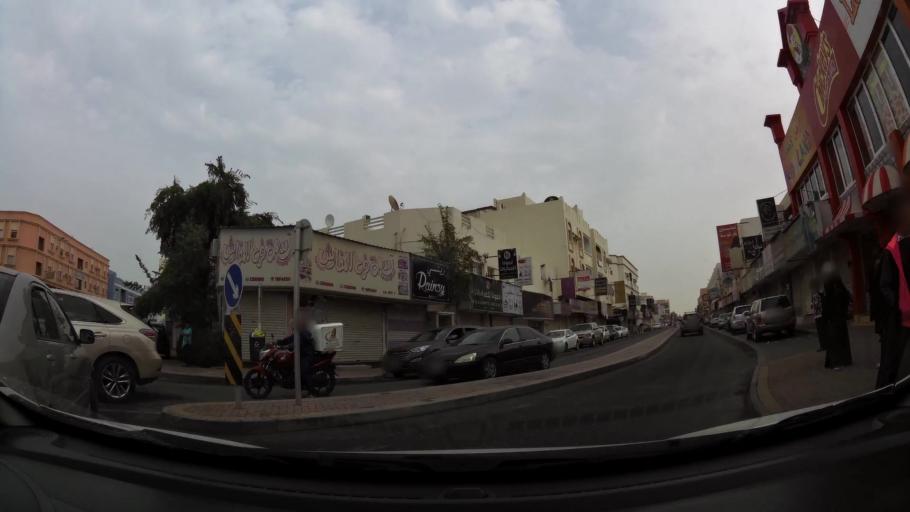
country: BH
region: Northern
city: Ar Rifa'
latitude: 26.1328
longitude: 50.5529
